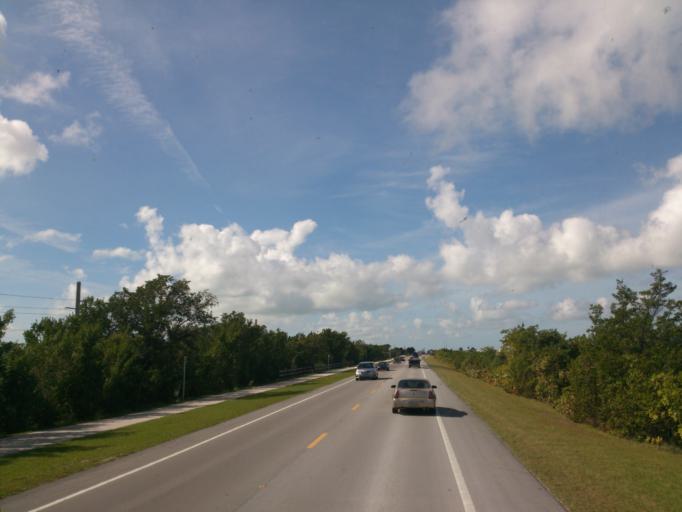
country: US
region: Florida
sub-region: Monroe County
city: Big Pine Key
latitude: 24.6688
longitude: -81.3760
